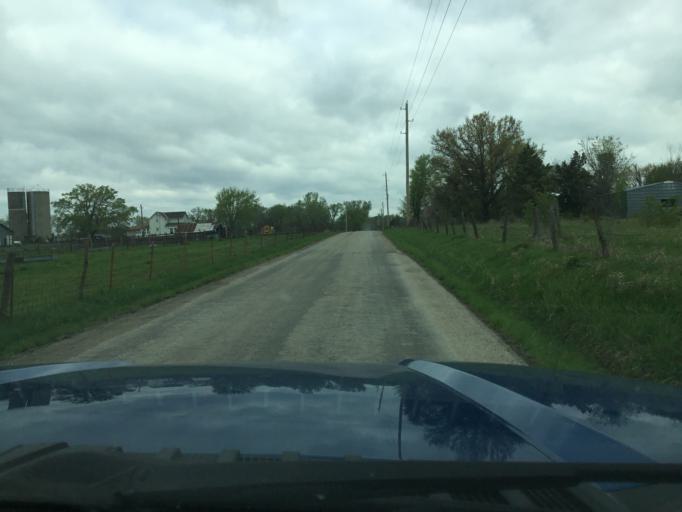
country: US
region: Kansas
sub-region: Douglas County
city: Lawrence
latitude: 38.9330
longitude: -95.1862
